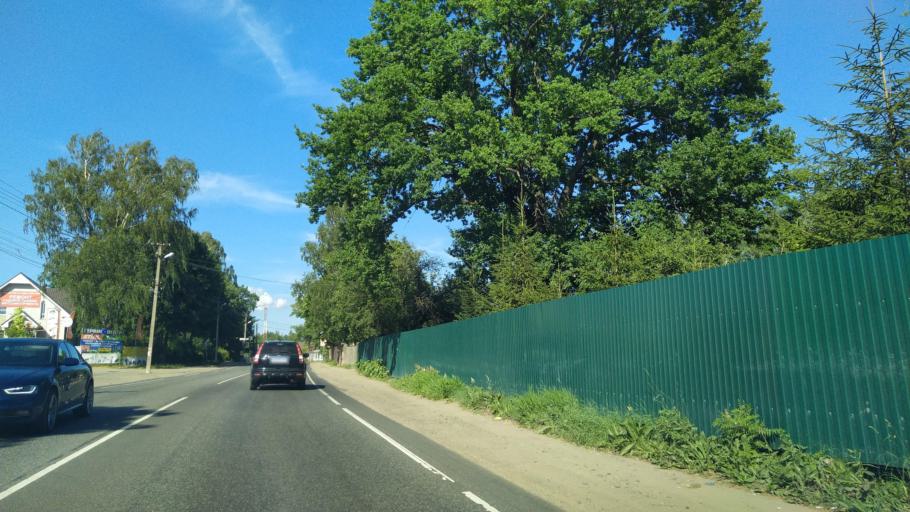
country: RU
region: Leningrad
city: Toksovo
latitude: 60.1617
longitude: 30.5371
